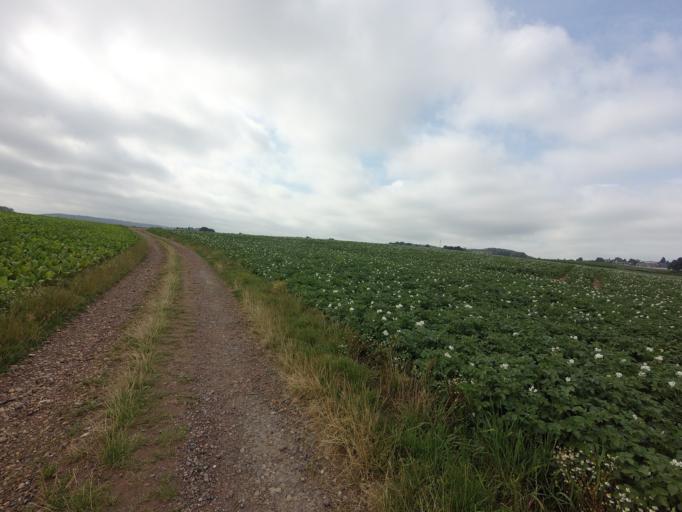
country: NL
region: Limburg
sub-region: Gemeente Simpelveld
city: Simpelveld
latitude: 50.7896
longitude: 5.9750
